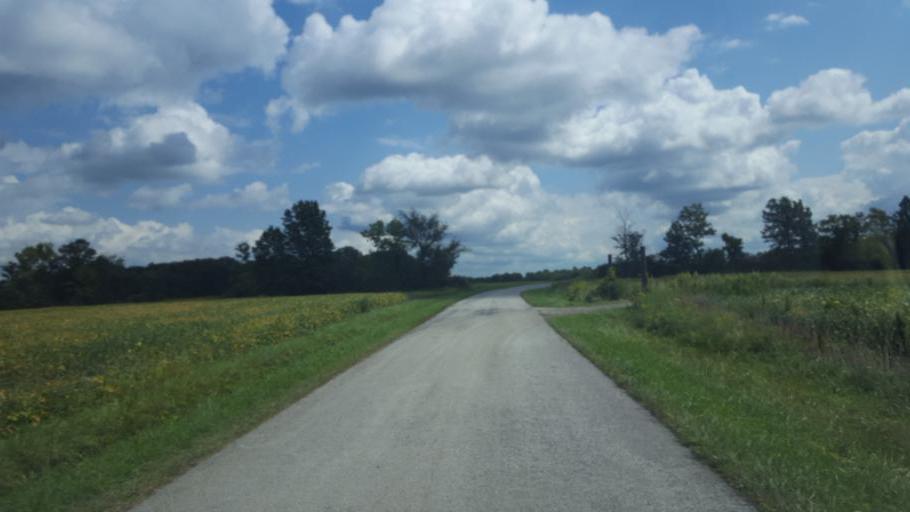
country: US
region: Ohio
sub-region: Huron County
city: Monroeville
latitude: 41.1683
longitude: -82.7195
